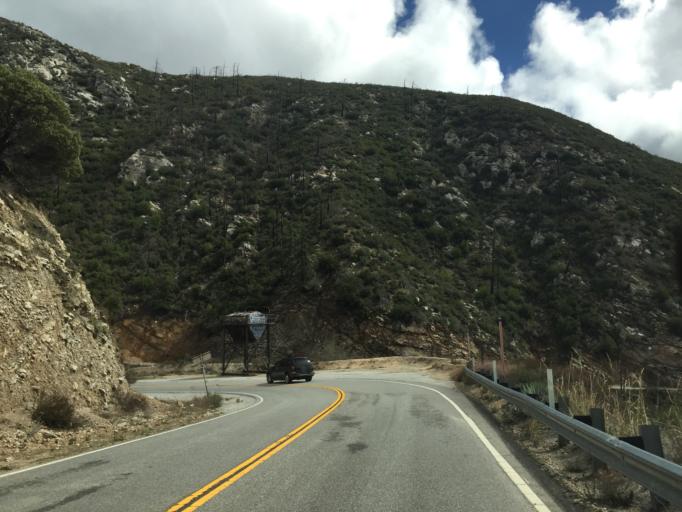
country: US
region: California
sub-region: Los Angeles County
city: Glendora
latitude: 34.2996
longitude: -117.8360
